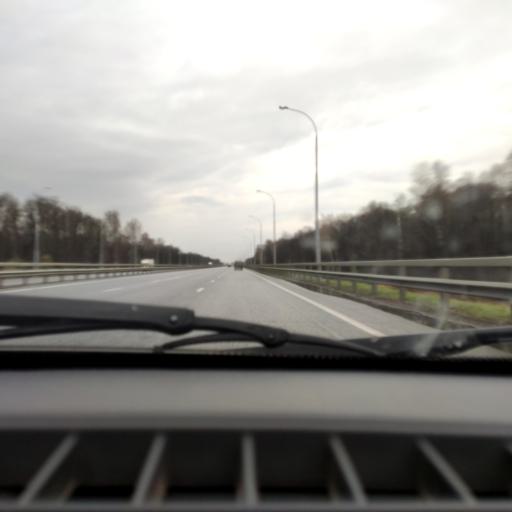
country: RU
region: Bashkortostan
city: Ufa
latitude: 54.6493
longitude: 56.0516
